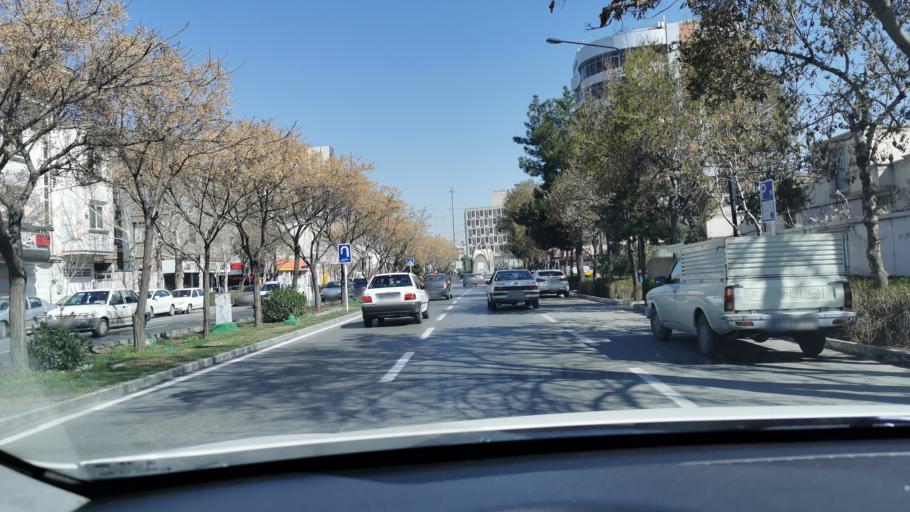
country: IR
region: Razavi Khorasan
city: Mashhad
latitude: 36.2952
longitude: 59.5729
